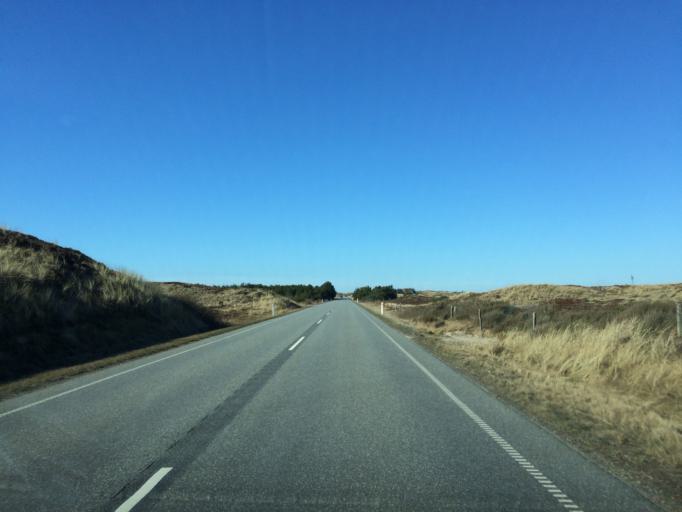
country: DK
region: Central Jutland
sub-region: Ringkobing-Skjern Kommune
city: Hvide Sande
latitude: 55.8955
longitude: 8.1704
